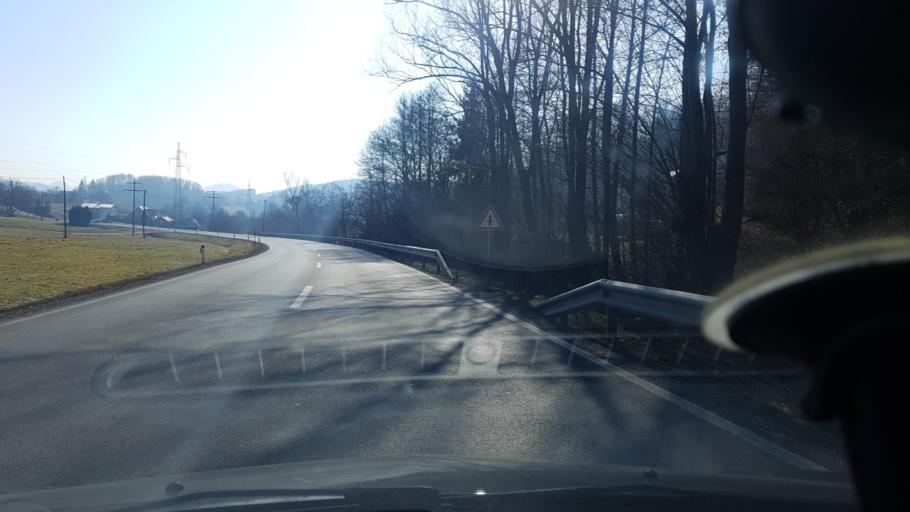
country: SI
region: Rogaska Slatina
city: Rogaska Slatina
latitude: 46.2447
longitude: 15.6531
